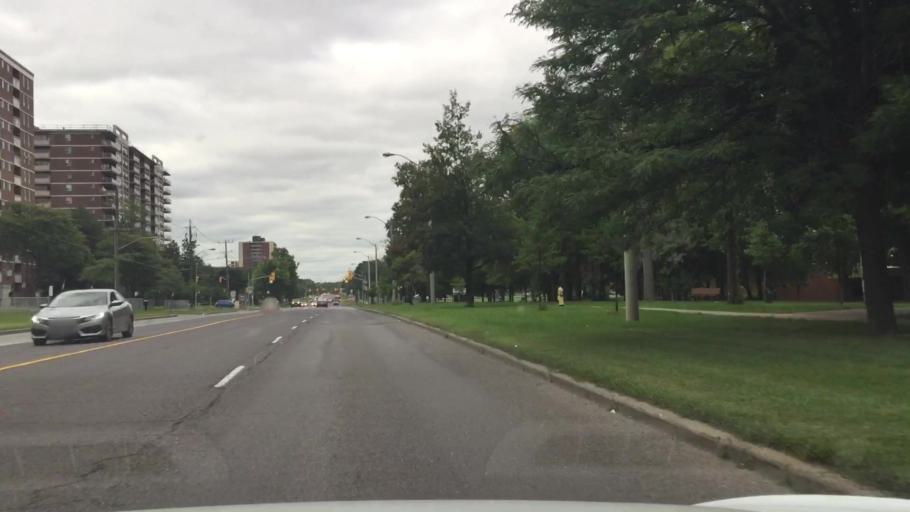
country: CA
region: Ontario
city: Concord
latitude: 43.7644
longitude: -79.5193
